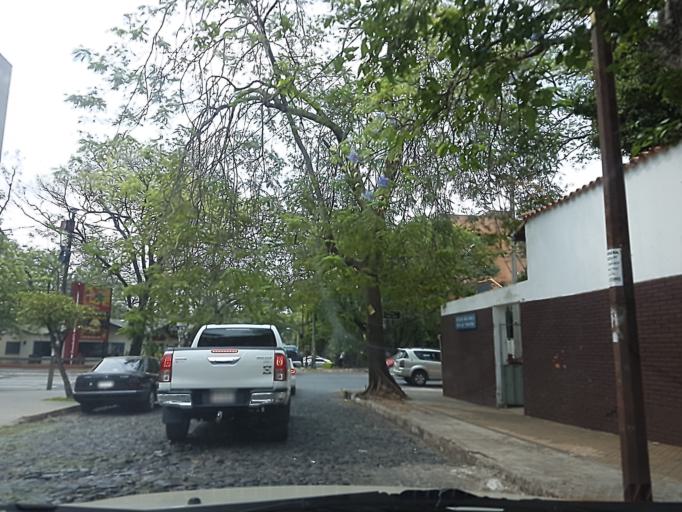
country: PY
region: Asuncion
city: Asuncion
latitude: -25.2928
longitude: -57.5836
